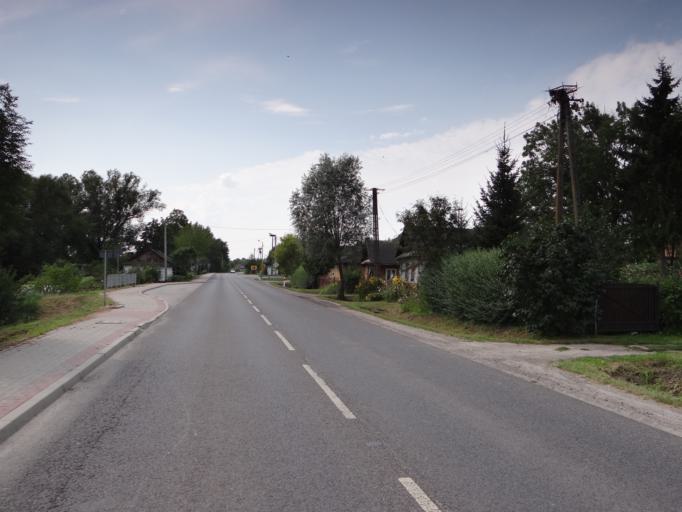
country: PL
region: Lublin Voivodeship
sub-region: Powiat hrubieszowski
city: Horodlo
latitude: 50.8423
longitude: 24.0246
